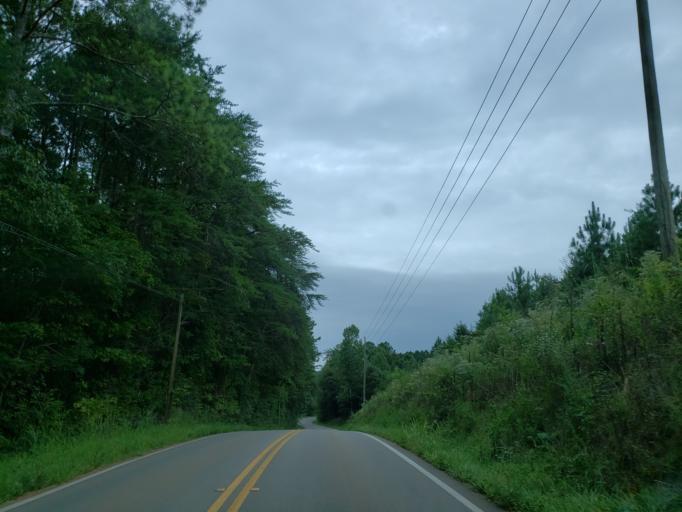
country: US
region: Georgia
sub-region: Pickens County
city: Jasper
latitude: 34.4206
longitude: -84.5762
